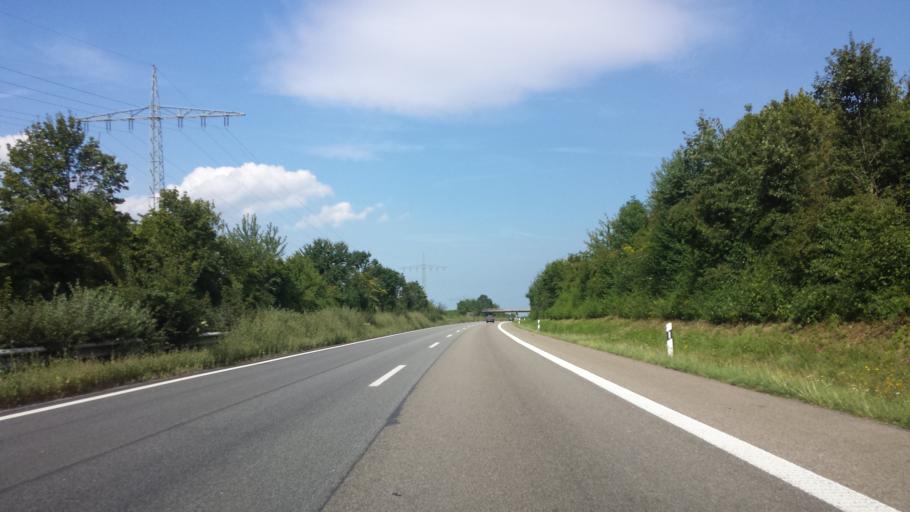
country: DE
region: Rheinland-Pfalz
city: Kirrweiler
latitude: 49.3050
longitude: 8.1547
